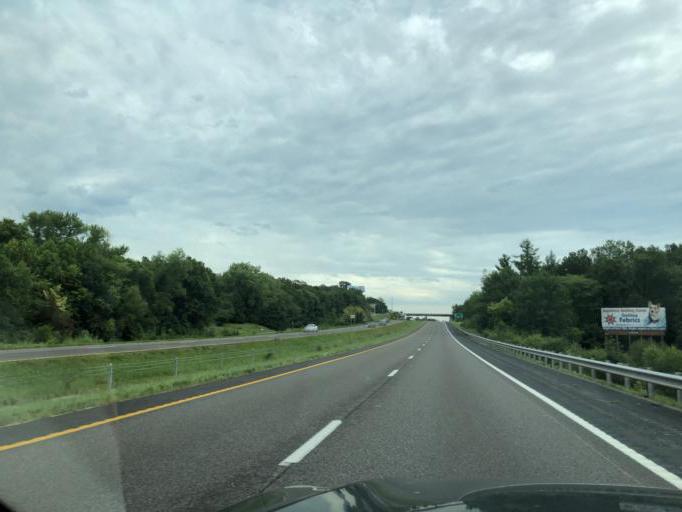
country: US
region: Missouri
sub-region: Boone County
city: Columbia
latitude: 38.9709
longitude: -92.4063
